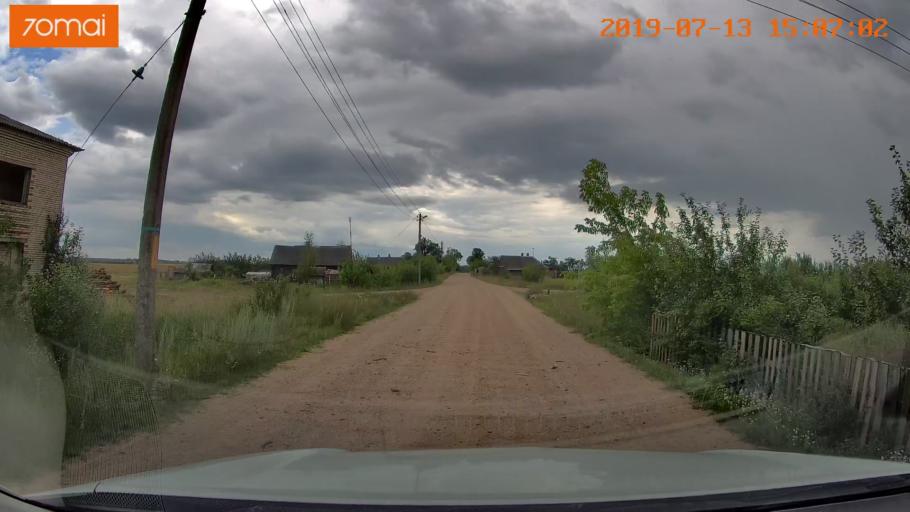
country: BY
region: Mogilev
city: Hlusha
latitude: 53.1939
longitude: 28.7566
